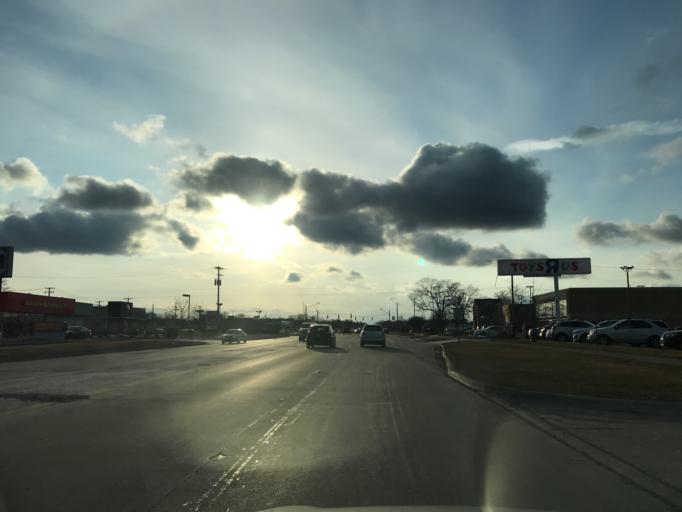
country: US
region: Michigan
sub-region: Oakland County
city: Farmington
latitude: 42.4273
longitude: -83.3331
